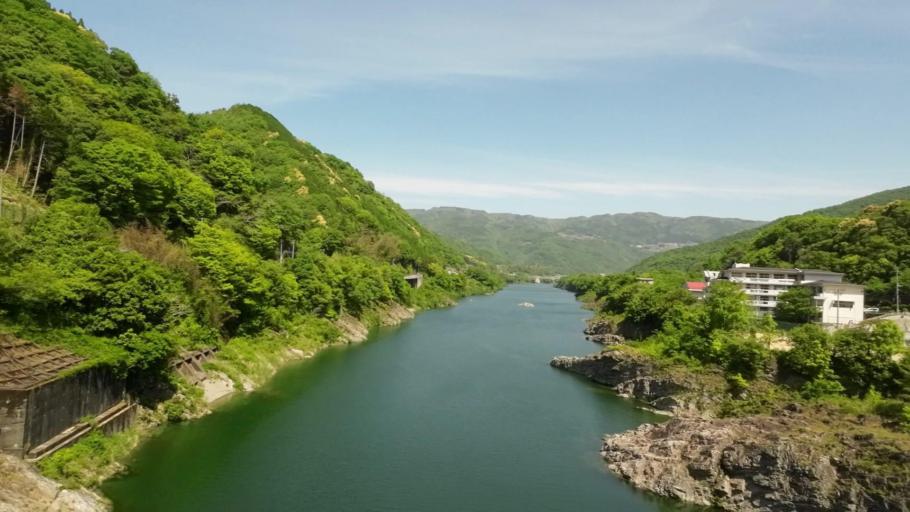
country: JP
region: Tokushima
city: Ikedacho
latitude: 33.9949
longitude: 133.7926
